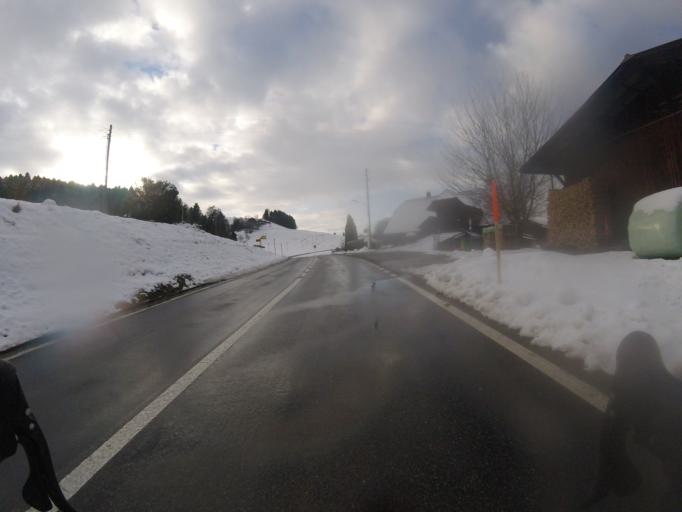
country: CH
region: Bern
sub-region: Bern-Mittelland District
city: Koniz
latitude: 46.8769
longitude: 7.4226
